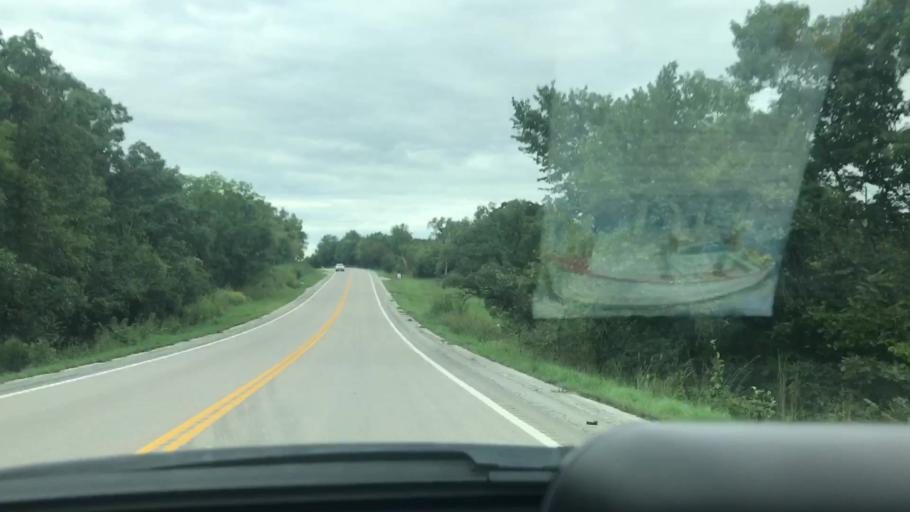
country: US
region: Missouri
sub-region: Benton County
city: Warsaw
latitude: 38.1673
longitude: -93.3091
